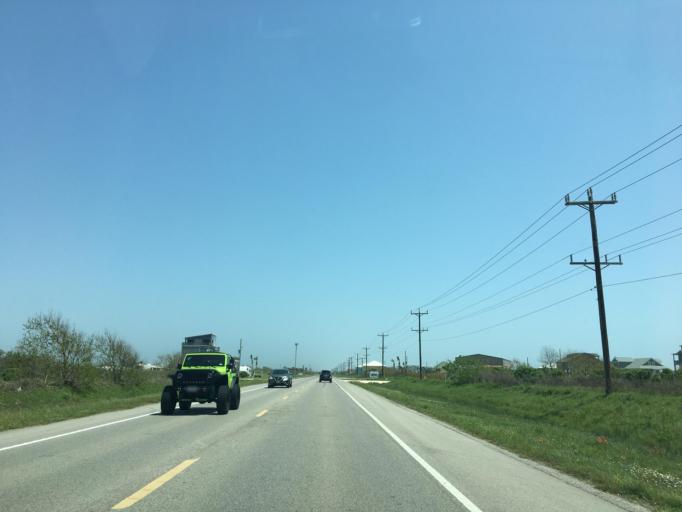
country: US
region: Texas
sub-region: Galveston County
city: Bolivar Peninsula
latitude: 29.4916
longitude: -94.5464
